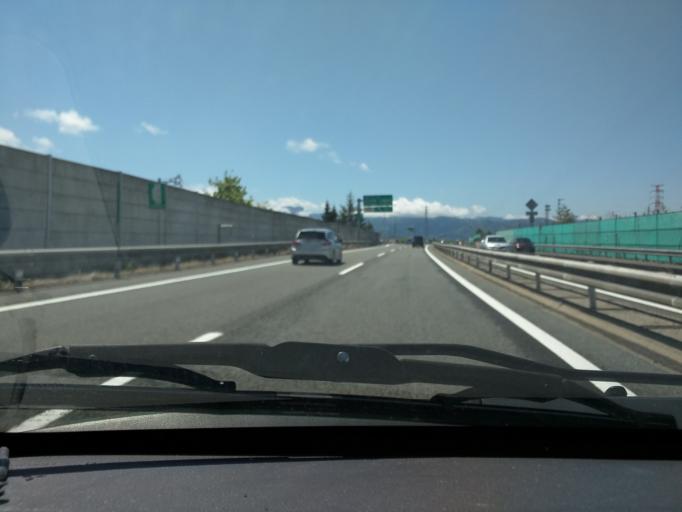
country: JP
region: Nagano
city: Nakano
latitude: 36.7339
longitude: 138.3180
